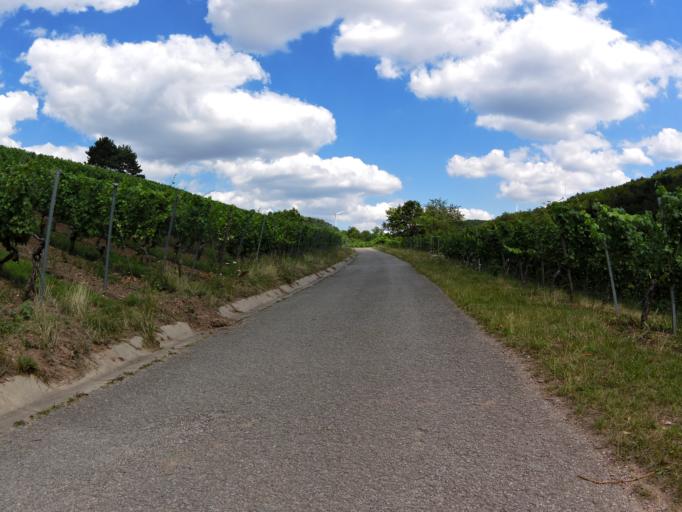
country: DE
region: Bavaria
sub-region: Regierungsbezirk Unterfranken
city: Thungersheim
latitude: 49.8795
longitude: 9.8592
